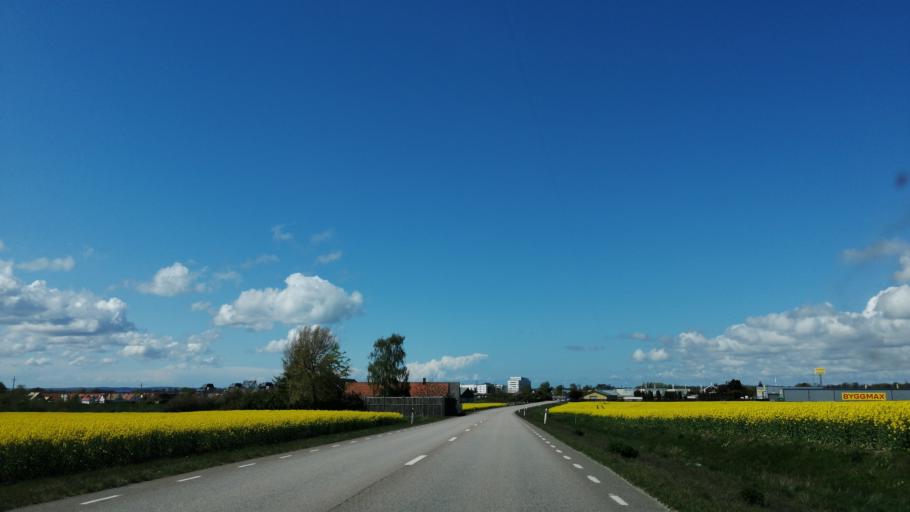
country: SE
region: Skane
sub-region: Helsingborg
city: Gantofta
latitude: 55.9593
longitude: 12.7916
